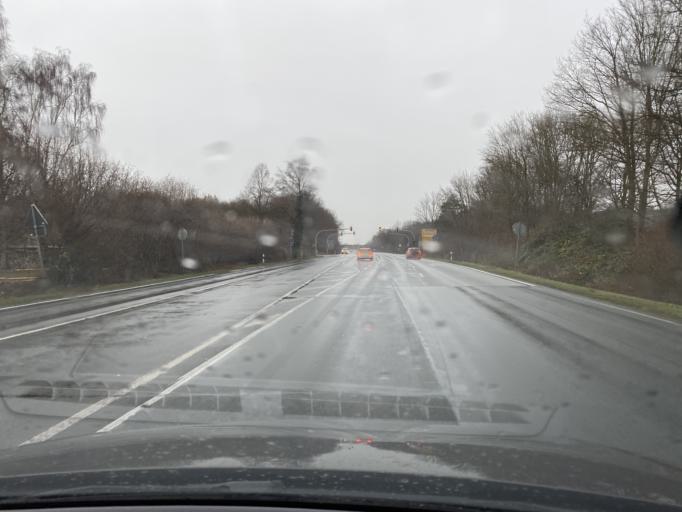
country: DE
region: North Rhine-Westphalia
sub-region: Regierungsbezirk Arnsberg
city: Lippstadt
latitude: 51.7104
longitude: 8.3560
